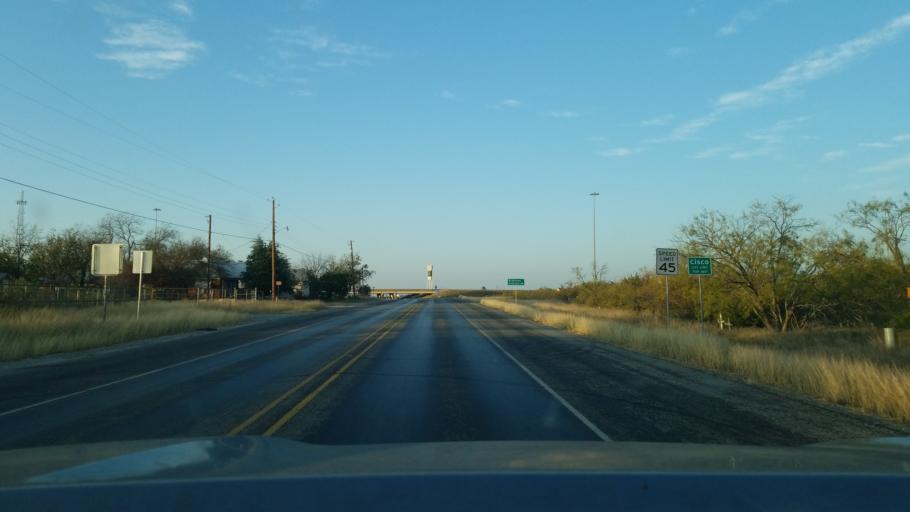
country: US
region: Texas
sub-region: Eastland County
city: Cisco
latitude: 32.3714
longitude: -98.9703
